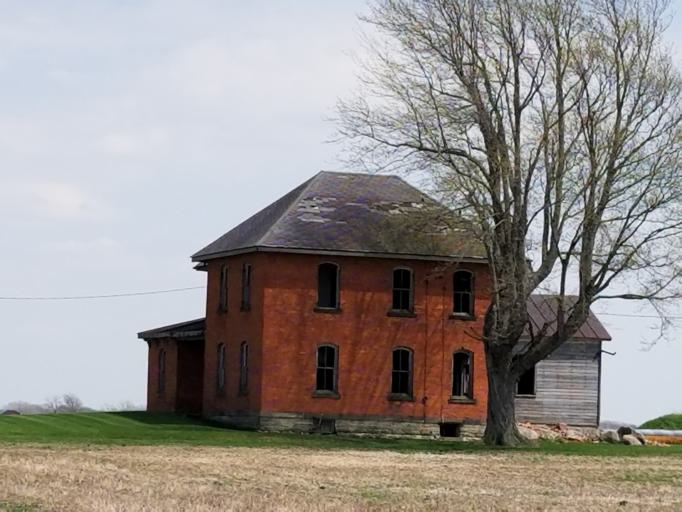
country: US
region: Ohio
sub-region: Huron County
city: Willard
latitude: 41.0106
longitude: -82.8114
